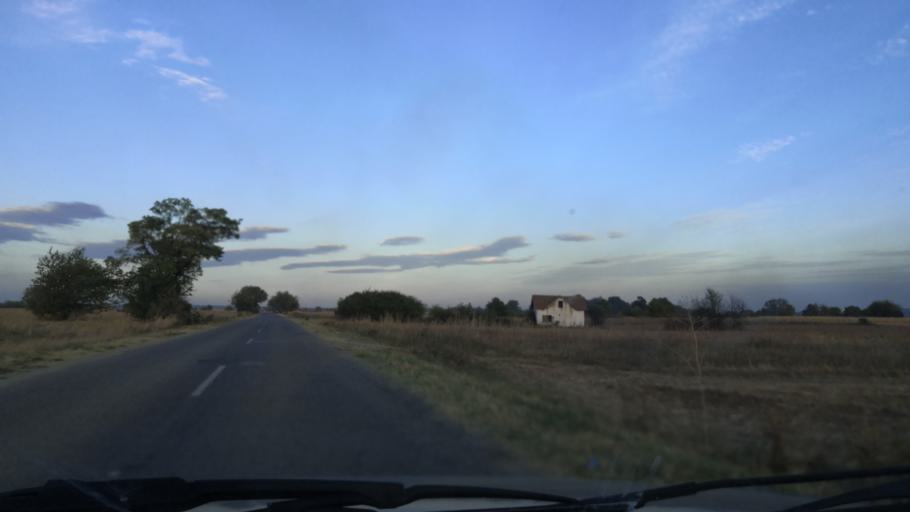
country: RS
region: Central Serbia
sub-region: Borski Okrug
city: Negotin
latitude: 44.2512
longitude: 22.5995
